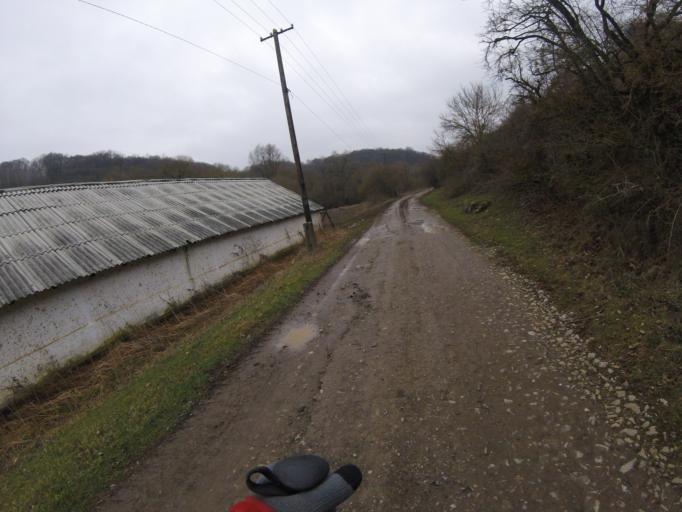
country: HU
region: Borsod-Abauj-Zemplen
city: Rudabanya
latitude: 48.4448
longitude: 20.5813
